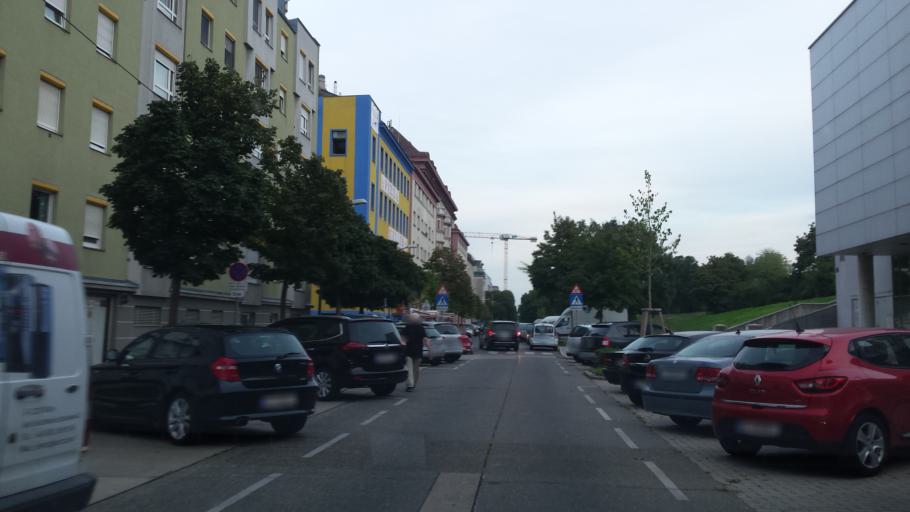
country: AT
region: Vienna
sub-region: Wien Stadt
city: Vienna
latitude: 48.2265
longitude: 16.4194
